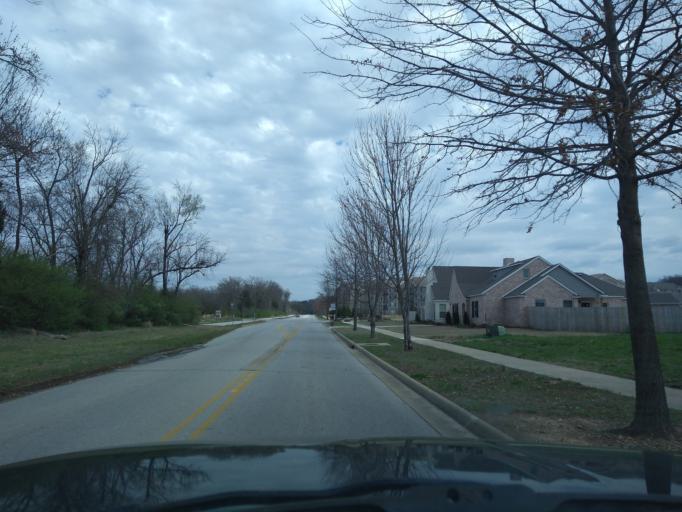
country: US
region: Arkansas
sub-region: Washington County
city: Farmington
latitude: 36.0711
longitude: -94.2121
